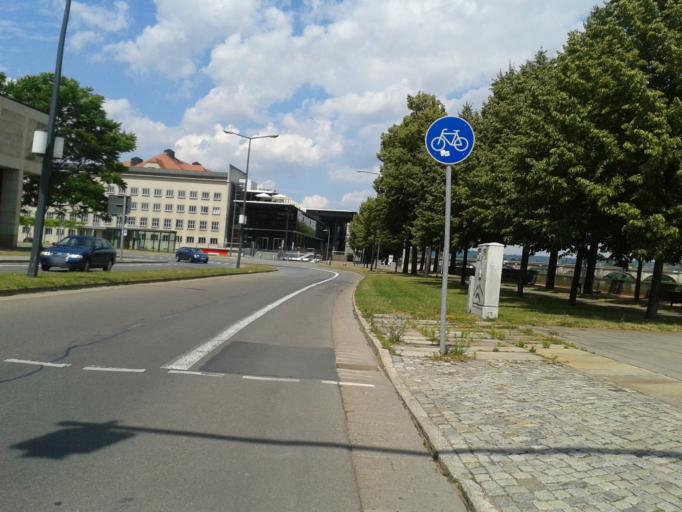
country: DE
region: Saxony
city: Dresden
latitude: 51.0555
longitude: 13.7356
